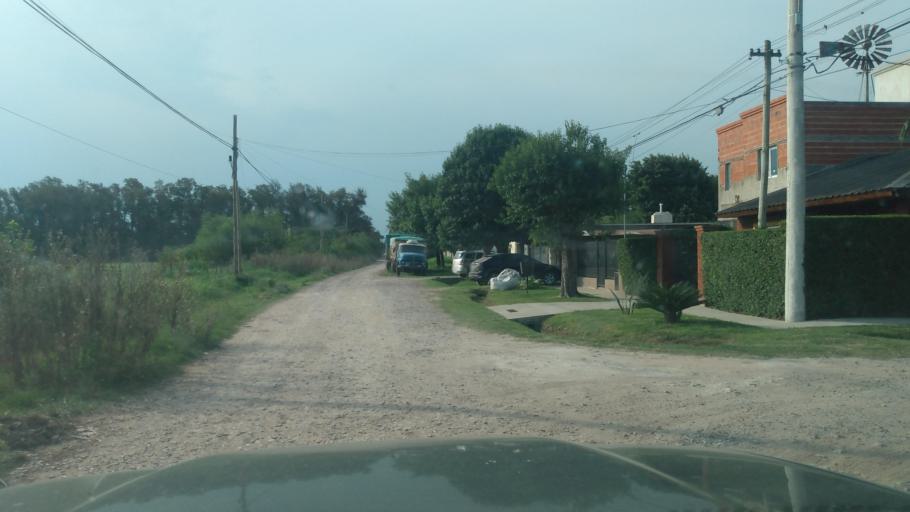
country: AR
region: Buenos Aires
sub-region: Partido de Lujan
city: Lujan
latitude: -34.5546
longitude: -59.1288
